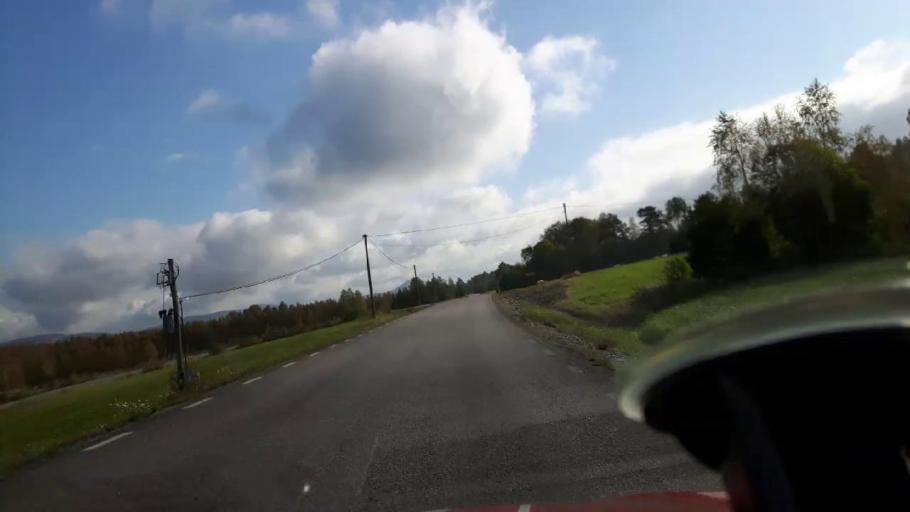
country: SE
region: Gaevleborg
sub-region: Ljusdals Kommun
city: Ljusdal
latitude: 61.7602
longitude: 16.0925
